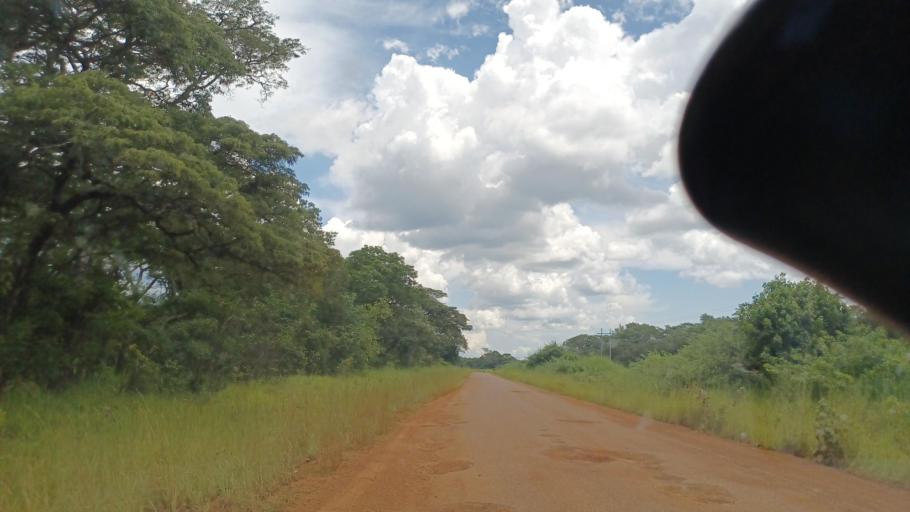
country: ZM
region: North-Western
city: Solwezi
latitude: -12.7137
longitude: 26.0236
